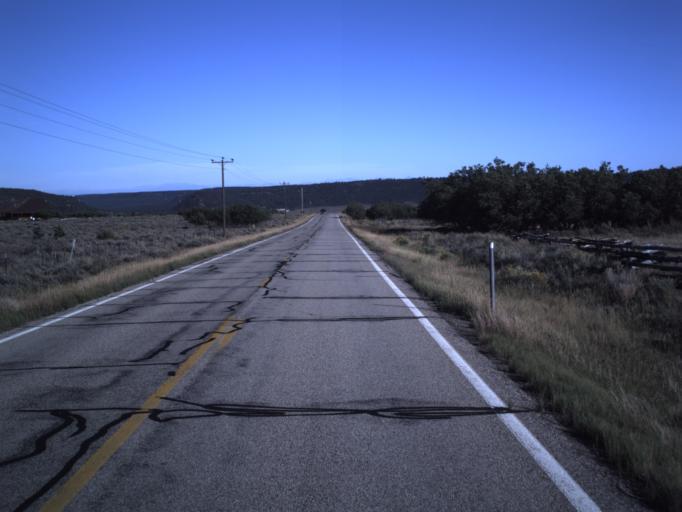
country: US
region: Utah
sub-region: Grand County
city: Moab
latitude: 38.3398
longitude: -109.1686
